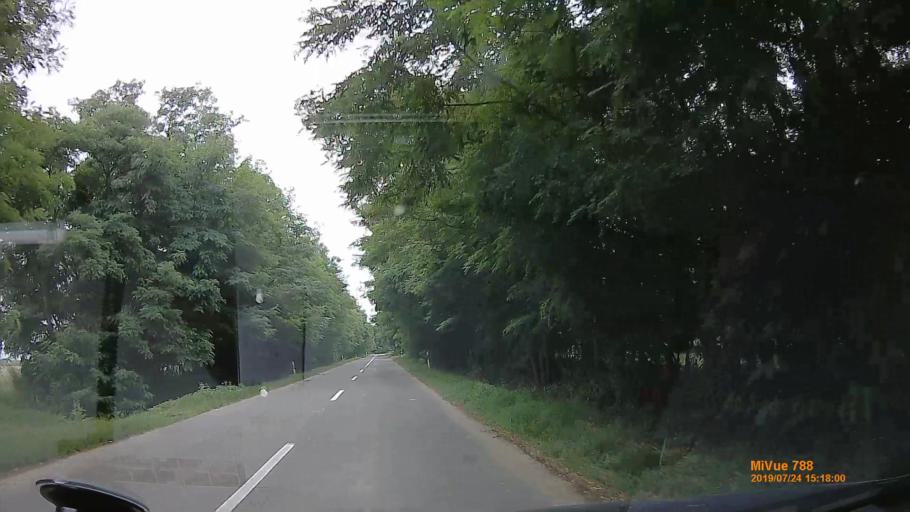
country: HU
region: Szabolcs-Szatmar-Bereg
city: Tarpa
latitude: 48.1860
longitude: 22.5487
